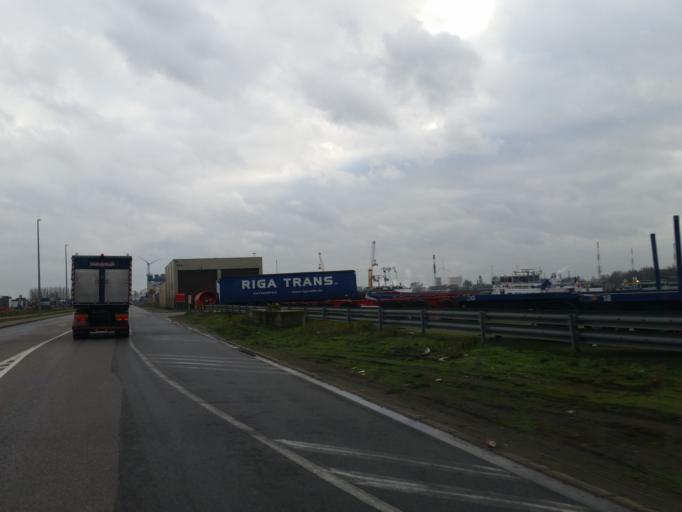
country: BE
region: Flanders
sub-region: Provincie Antwerpen
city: Stabroek
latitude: 51.3065
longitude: 4.3298
